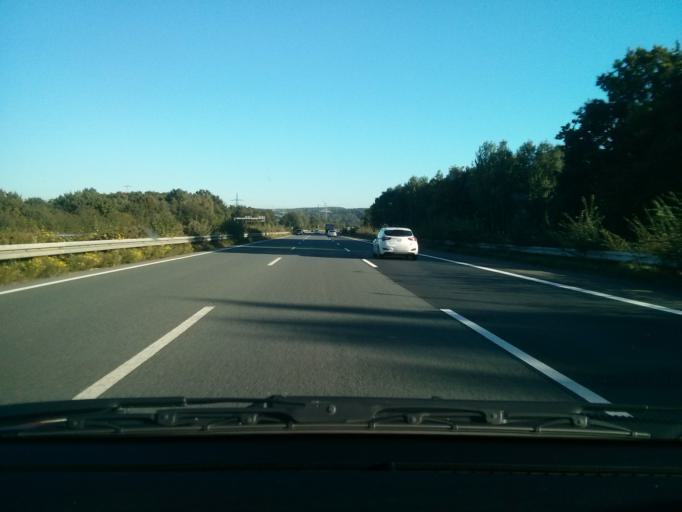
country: DE
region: North Rhine-Westphalia
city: Witten
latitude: 51.4659
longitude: 7.4090
